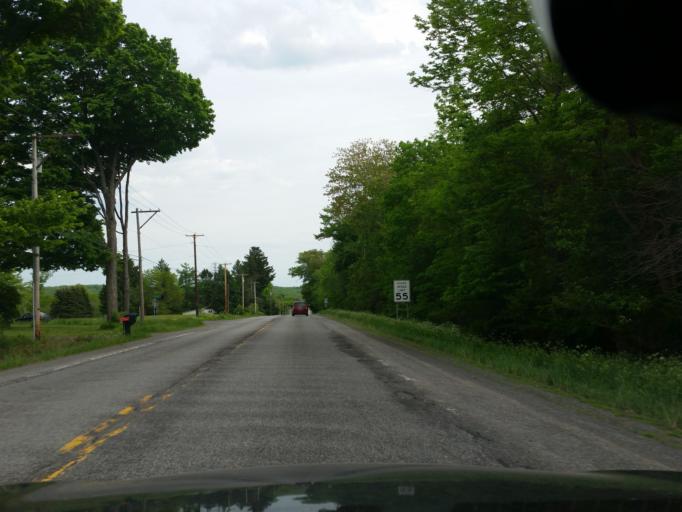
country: US
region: New York
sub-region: Chautauqua County
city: Mayville
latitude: 42.2102
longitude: -79.4257
